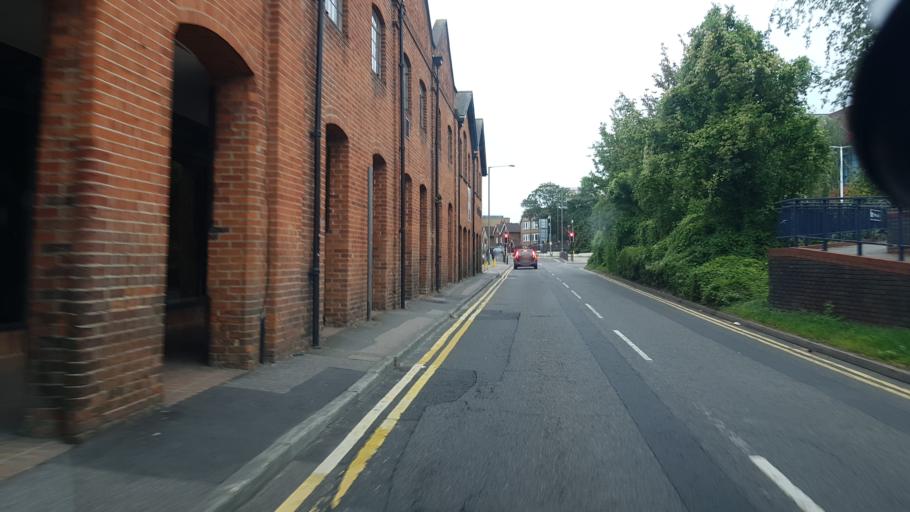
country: GB
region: England
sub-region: Surrey
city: Guildford
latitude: 51.2373
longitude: -0.5798
